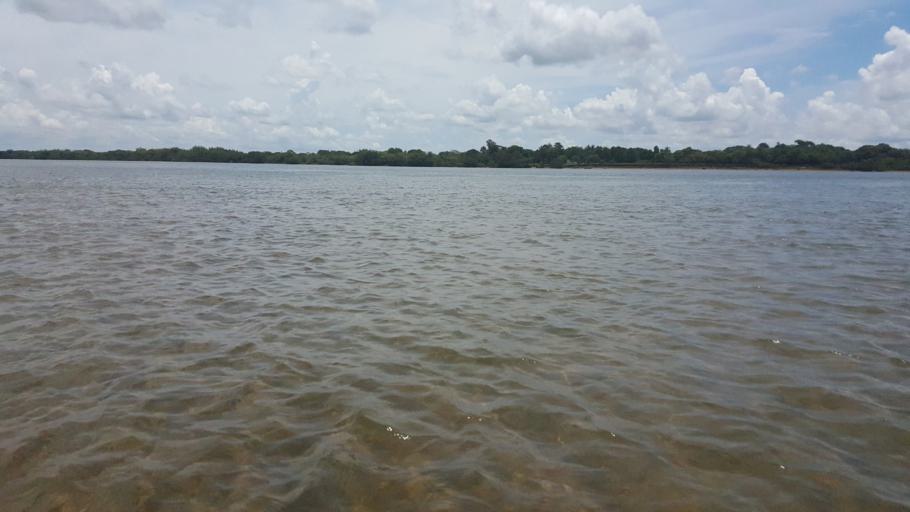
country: AR
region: Corrientes
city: Ituzaingo
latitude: -27.5742
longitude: -56.7058
